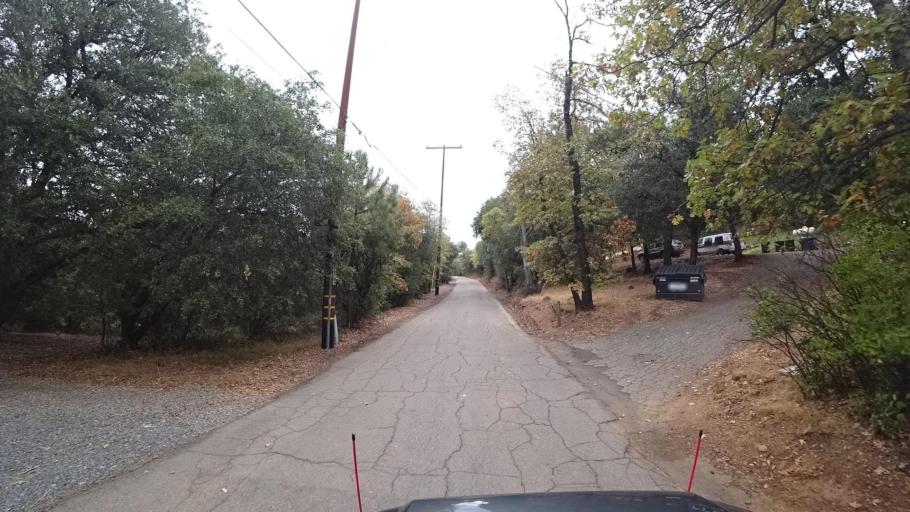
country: US
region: California
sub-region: San Diego County
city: Julian
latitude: 33.0500
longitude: -116.6257
